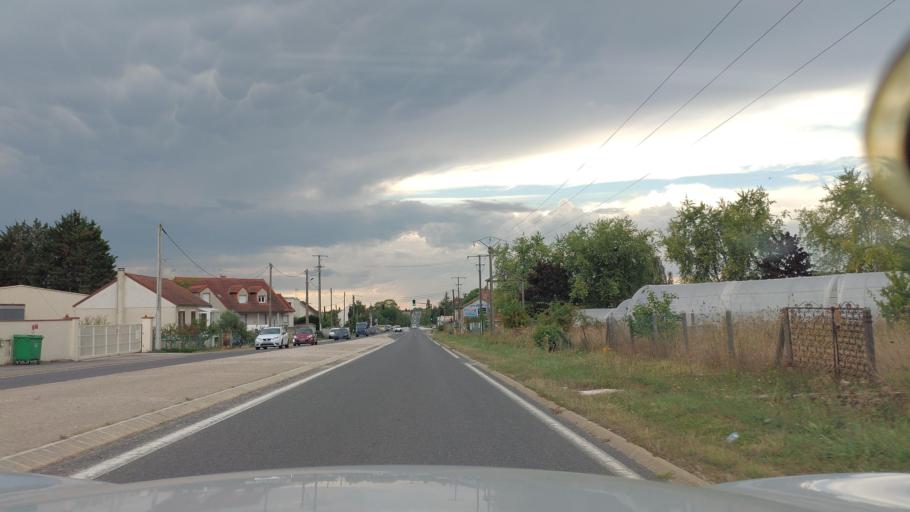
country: FR
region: Ile-de-France
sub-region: Departement de Seine-et-Marne
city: Grisy-Suisnes
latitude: 48.6781
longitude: 2.6603
